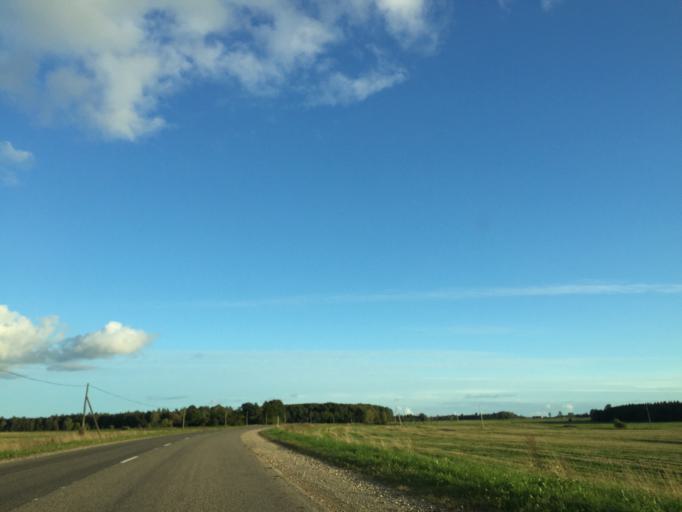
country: LV
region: Saldus Rajons
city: Saldus
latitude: 56.7479
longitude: 22.3757
